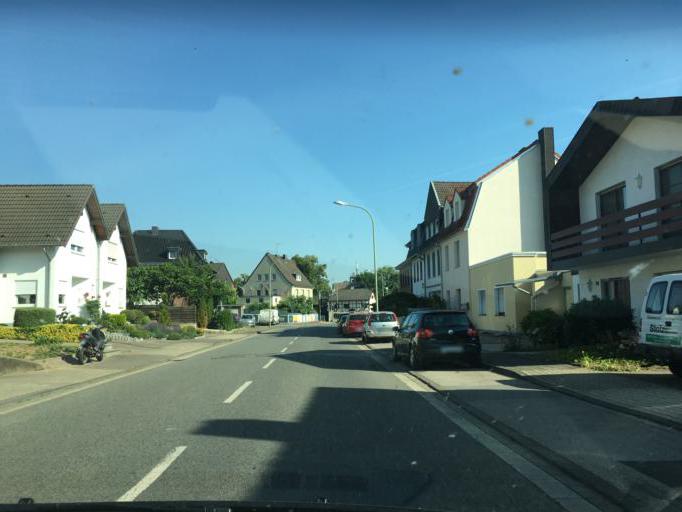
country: DE
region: North Rhine-Westphalia
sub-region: Regierungsbezirk Koln
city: Dueren
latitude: 50.7957
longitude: 6.4605
